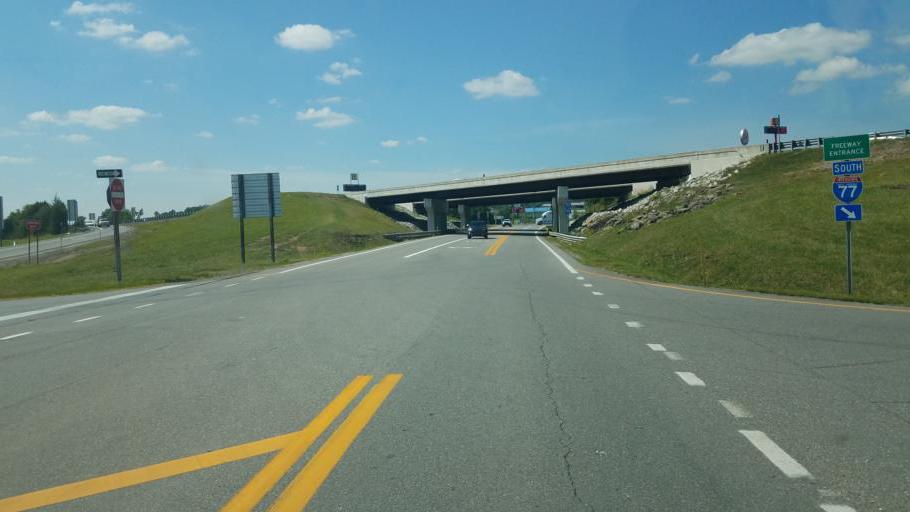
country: US
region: West Virginia
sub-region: Jackson County
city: Ripley
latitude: 38.7585
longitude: -81.6917
